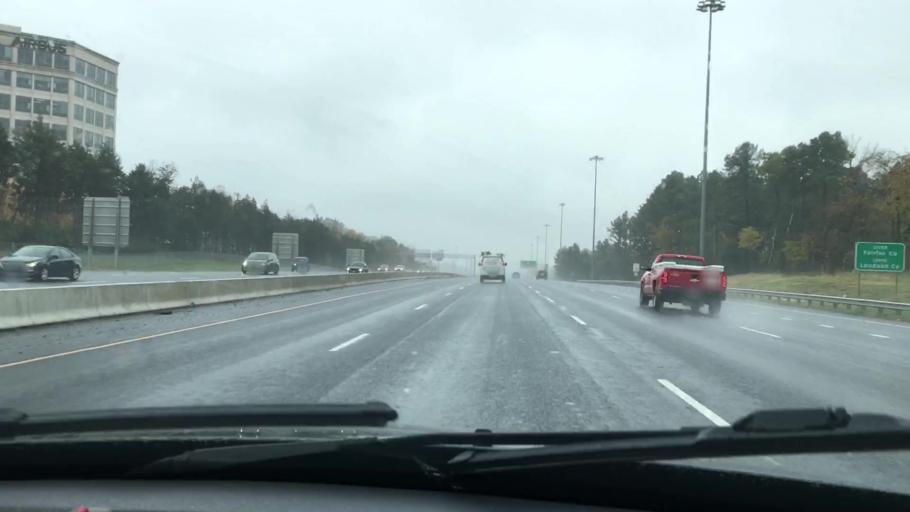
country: US
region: Virginia
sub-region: Fairfax County
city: Floris
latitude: 38.9554
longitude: -77.4296
